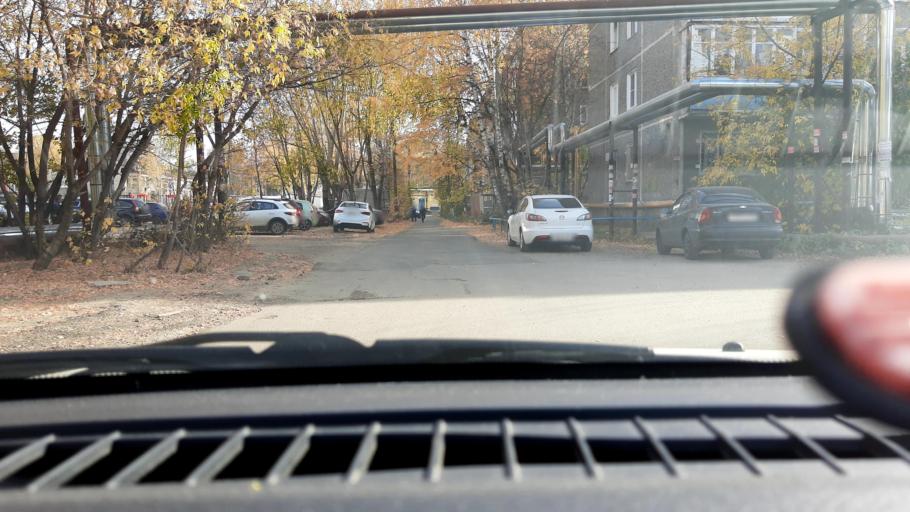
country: RU
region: Nizjnij Novgorod
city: Nizhniy Novgorod
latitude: 56.2808
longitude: 43.9165
